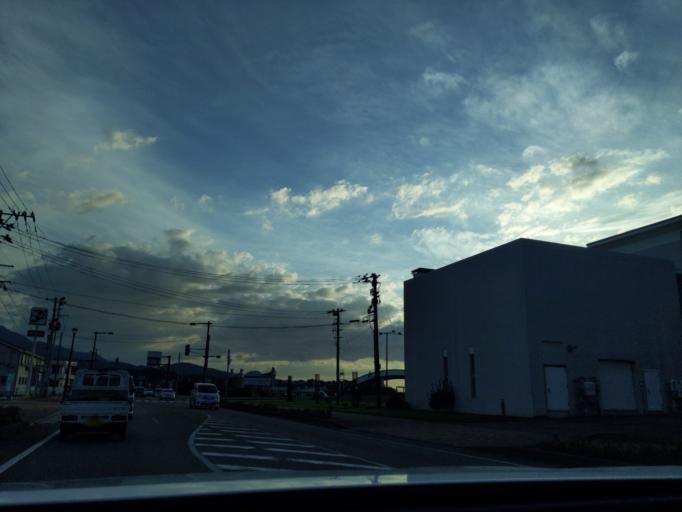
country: JP
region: Niigata
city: Kashiwazaki
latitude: 37.3712
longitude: 138.5476
